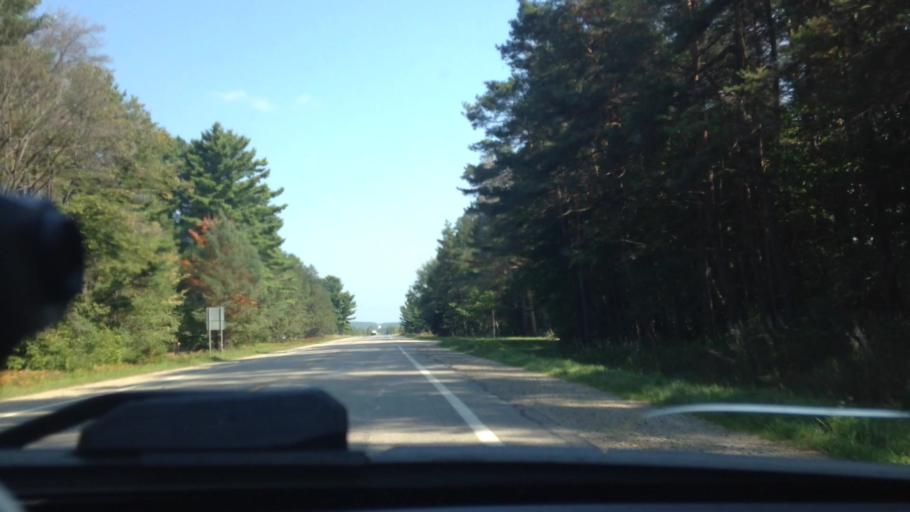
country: US
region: Michigan
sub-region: Luce County
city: Newberry
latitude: 46.3102
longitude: -85.6367
